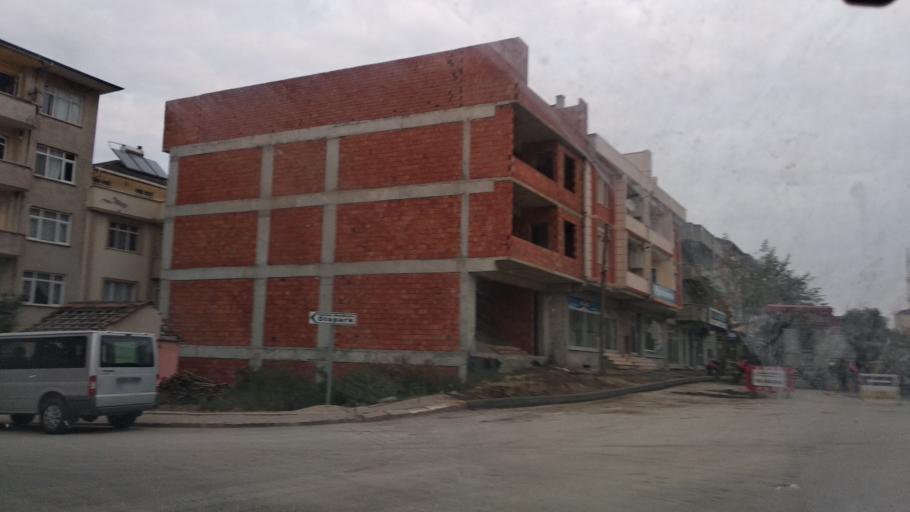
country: TR
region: Sakarya
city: Karasu
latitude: 41.0948
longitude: 30.6869
